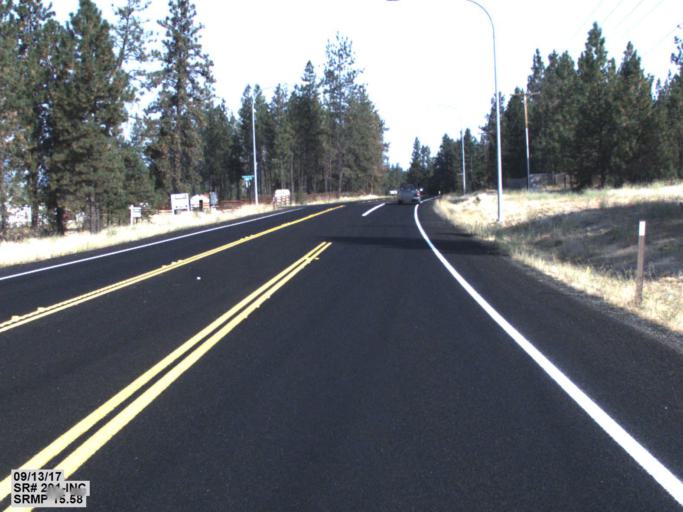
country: US
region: Washington
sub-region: Spokane County
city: Deer Park
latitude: 47.8338
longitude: -117.6035
